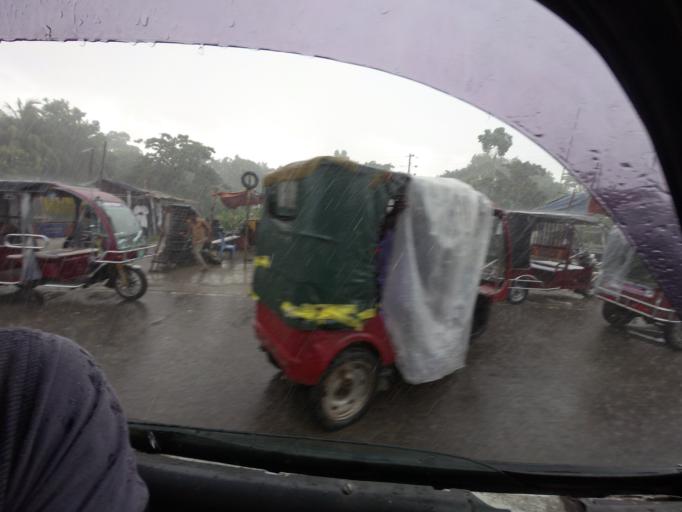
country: BD
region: Dhaka
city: Char Bhadrasan
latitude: 23.4034
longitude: 90.1513
